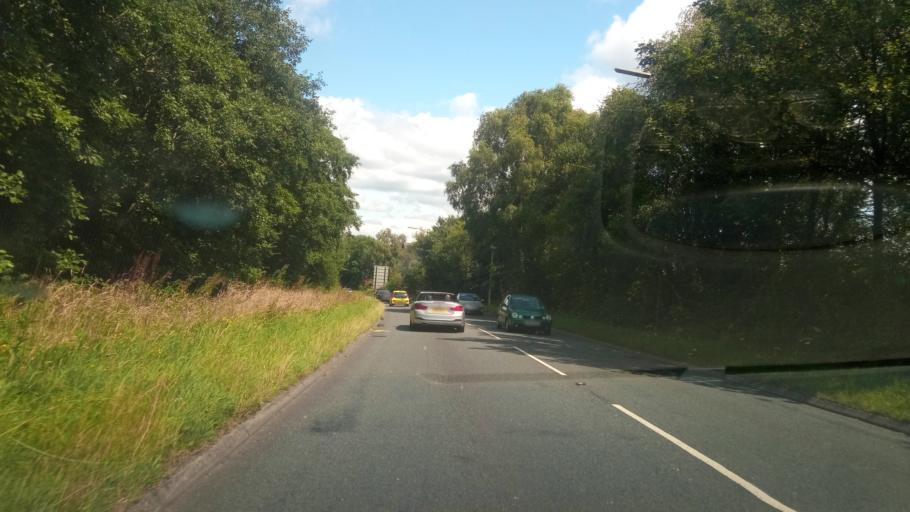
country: GB
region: Wales
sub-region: Caerphilly County Borough
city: Caerphilly
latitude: 51.5706
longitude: -3.2470
